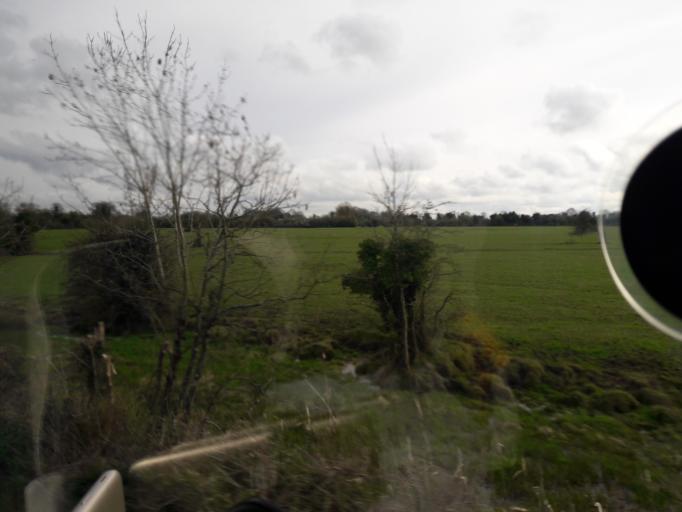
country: IE
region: Leinster
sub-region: An Mhi
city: Longwood
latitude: 53.4404
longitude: -6.9276
